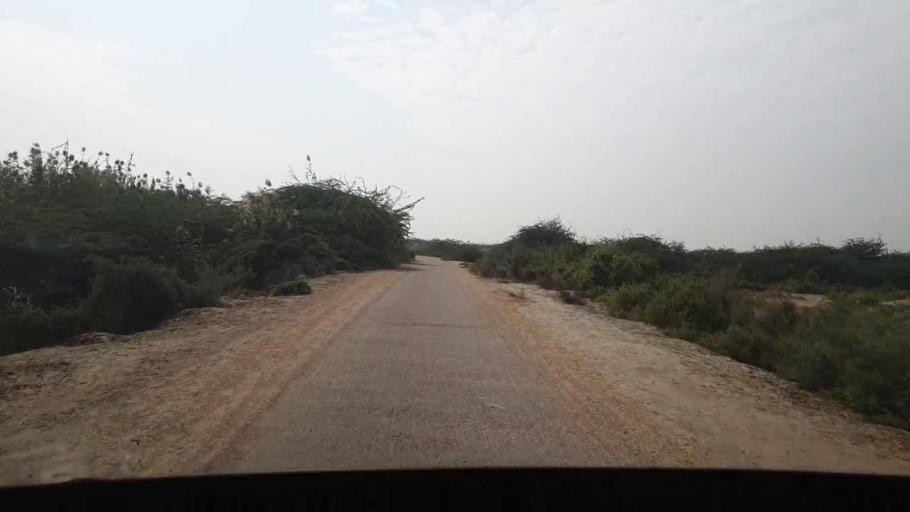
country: PK
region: Sindh
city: Chuhar Jamali
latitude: 24.2392
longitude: 67.9852
